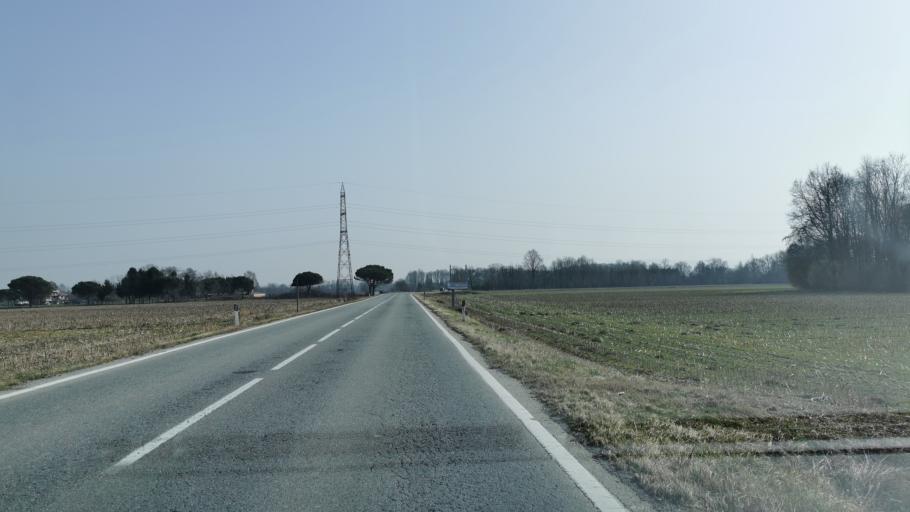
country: IT
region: Piedmont
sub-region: Provincia di Torino
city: San Benigno Canavese
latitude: 45.2196
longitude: 7.7642
